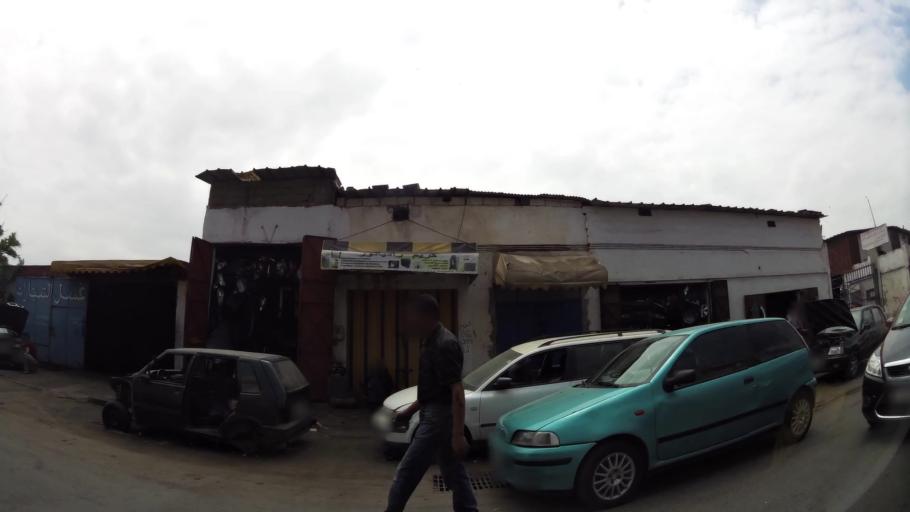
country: MA
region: Rabat-Sale-Zemmour-Zaer
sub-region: Skhirate-Temara
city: Temara
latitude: 33.9811
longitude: -6.8912
